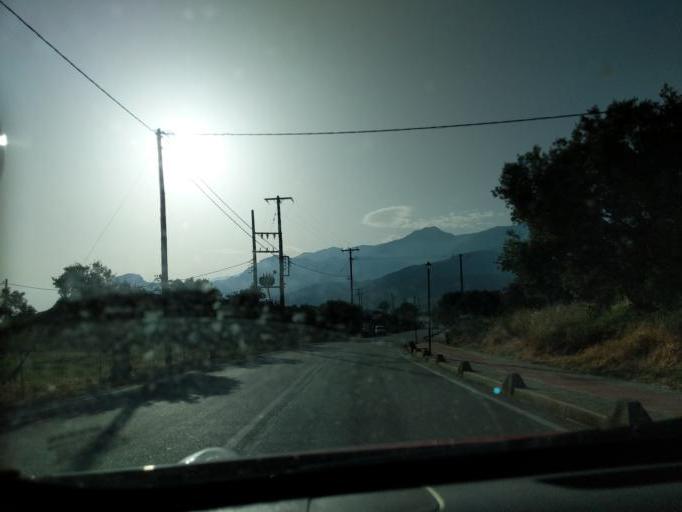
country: GR
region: Crete
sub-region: Nomos Rethymnis
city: Atsipopoulon
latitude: 35.1859
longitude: 24.4049
